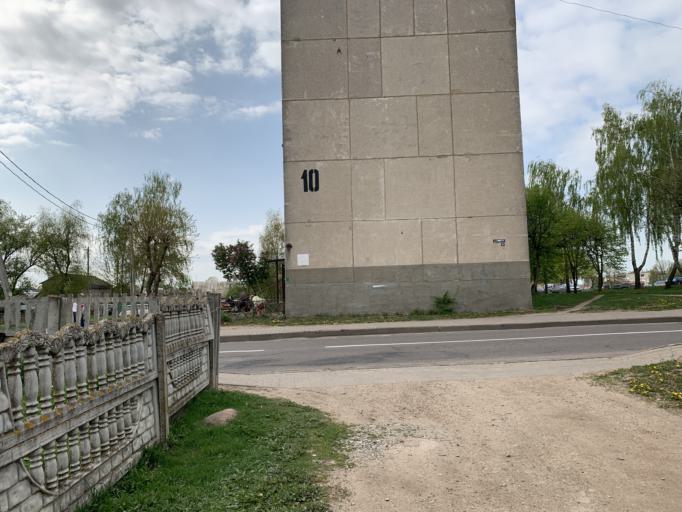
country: BY
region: Minsk
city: Nyasvizh
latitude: 53.2178
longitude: 26.6777
